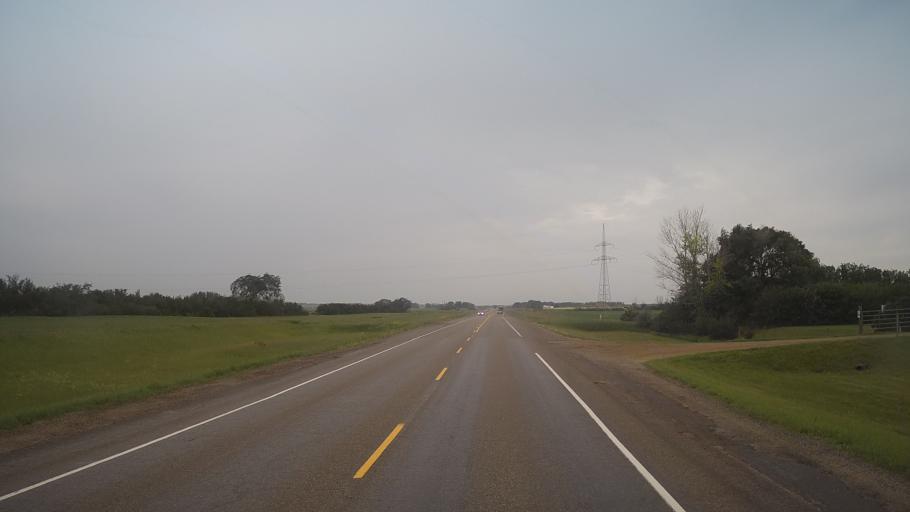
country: CA
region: Saskatchewan
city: Saskatoon
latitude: 52.1292
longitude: -106.8500
